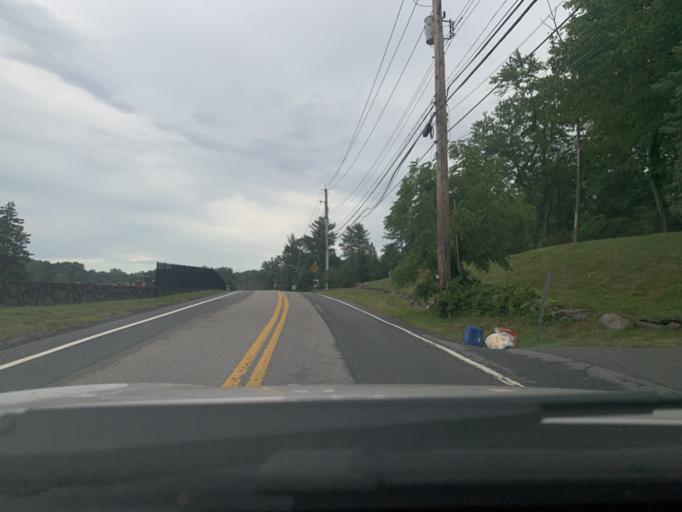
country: US
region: New York
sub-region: Westchester County
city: Ossining
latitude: 41.1792
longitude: -73.8515
